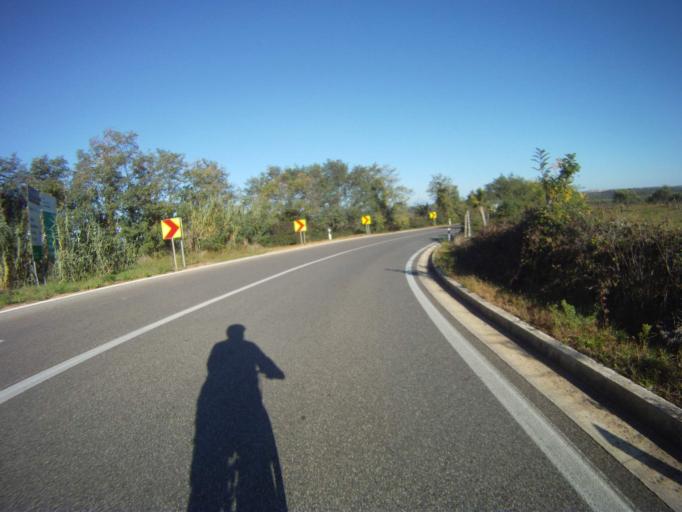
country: HR
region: Istarska
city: Novigrad
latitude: 45.3449
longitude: 13.5935
